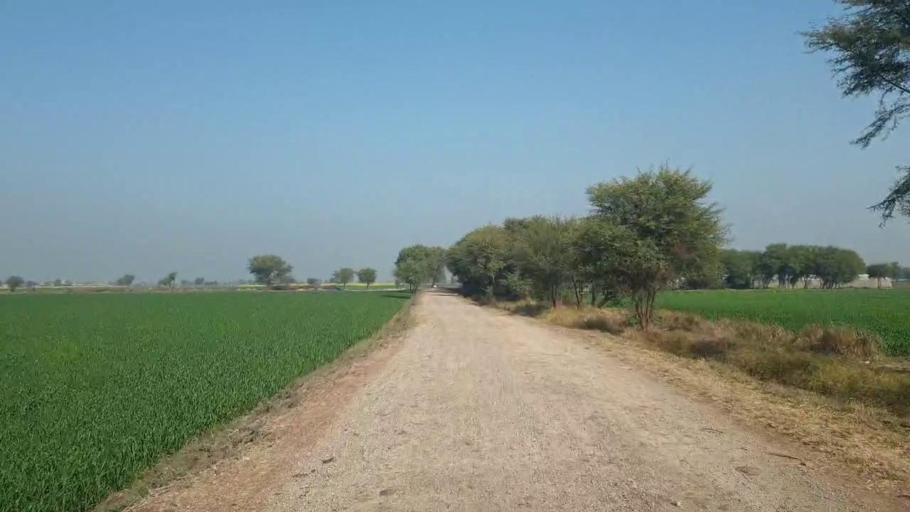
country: PK
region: Sindh
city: Shahdadpur
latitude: 25.9666
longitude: 68.5870
